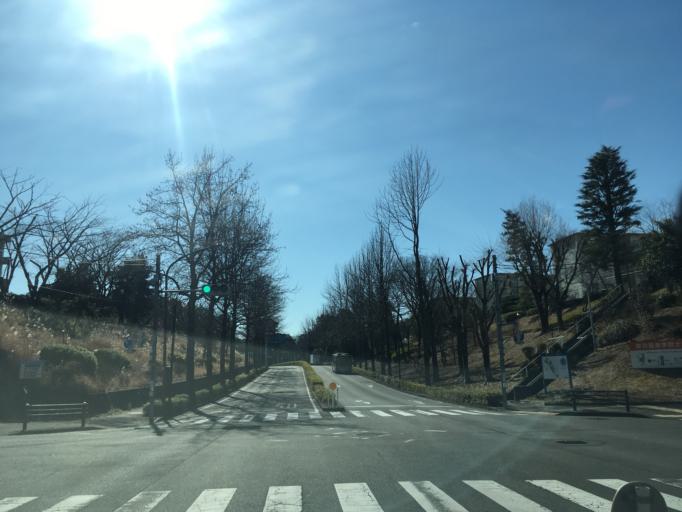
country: JP
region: Tokyo
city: Hino
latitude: 35.6123
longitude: 139.4323
